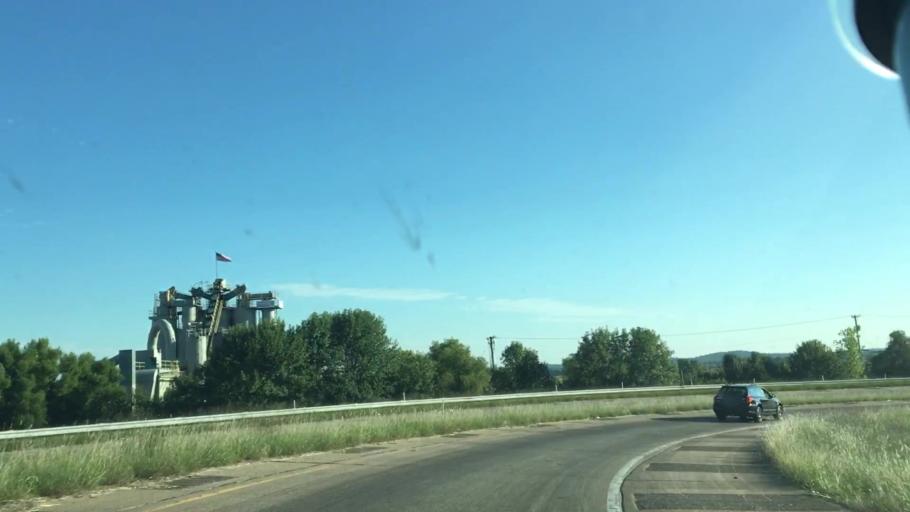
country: US
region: Indiana
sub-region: Vanderburgh County
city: Evansville
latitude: 37.9387
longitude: -87.4914
